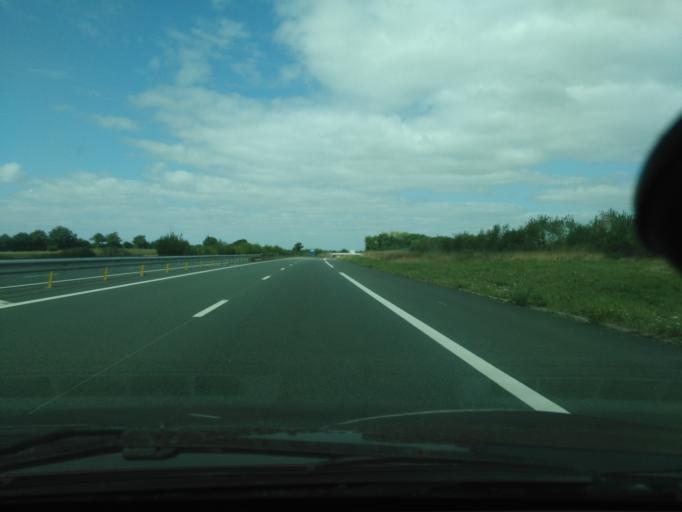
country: FR
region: Pays de la Loire
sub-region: Departement de la Vendee
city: Les Clouzeaux
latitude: 46.6349
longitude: -1.4871
